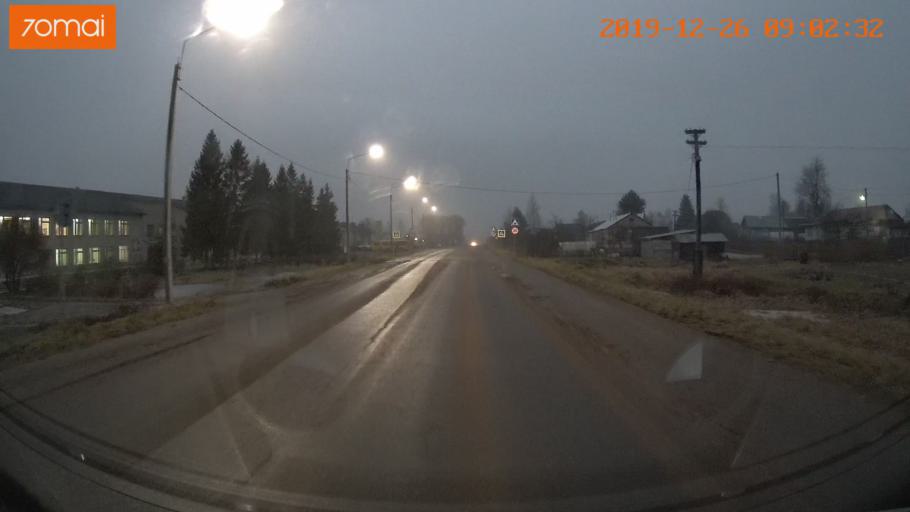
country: RU
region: Vologda
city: Gryazovets
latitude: 58.7966
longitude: 40.2662
